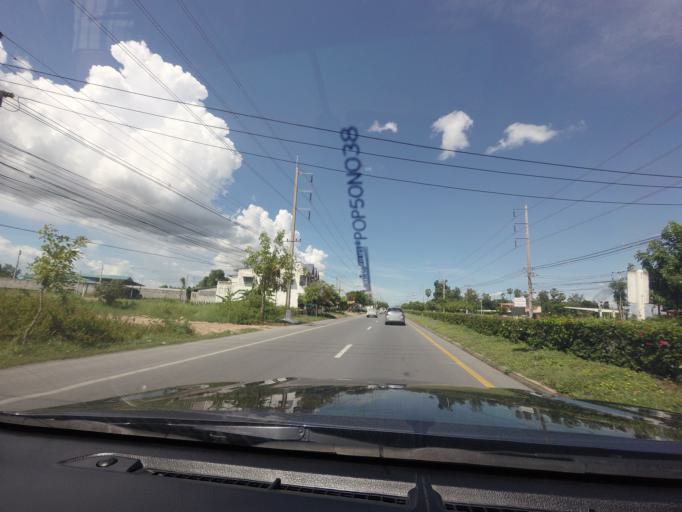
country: TH
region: Kanchanaburi
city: Phanom Thuan
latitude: 14.0645
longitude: 99.6381
